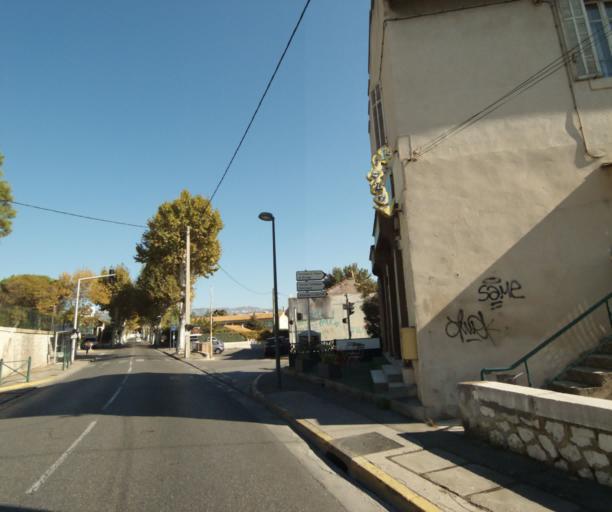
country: FR
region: Provence-Alpes-Cote d'Azur
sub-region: Departement des Bouches-du-Rhone
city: Plan-de-Cuques
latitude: 43.3404
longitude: 5.4566
